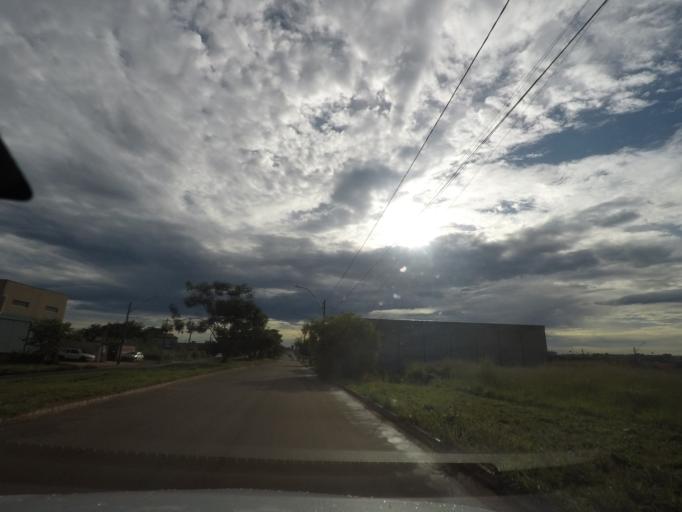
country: BR
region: Goias
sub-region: Aparecida De Goiania
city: Aparecida de Goiania
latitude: -16.7623
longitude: -49.3616
